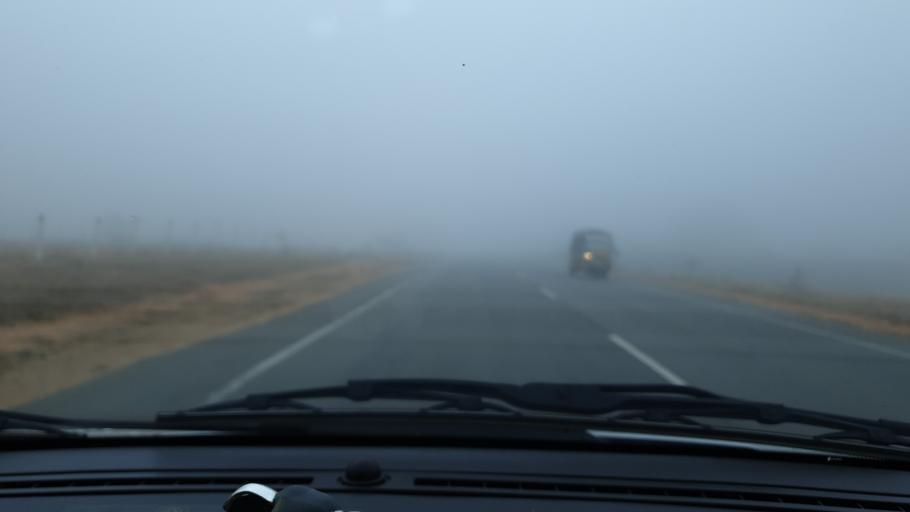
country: IN
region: Telangana
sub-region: Mahbubnagar
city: Nagar Karnul
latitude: 16.6813
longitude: 78.5262
